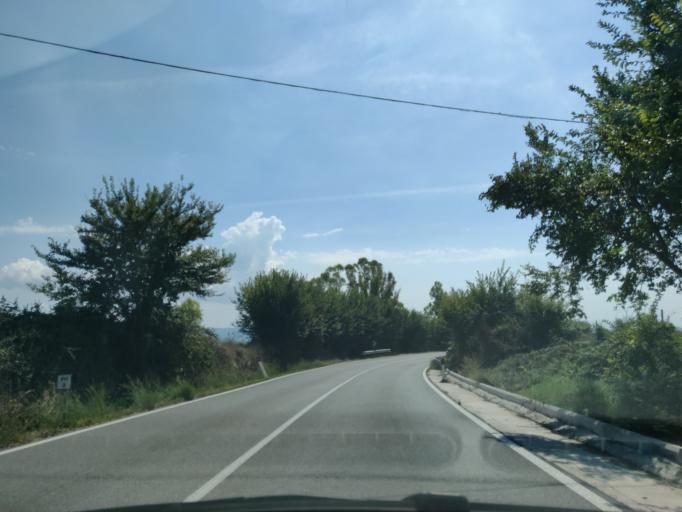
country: IT
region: Latium
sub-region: Provincia di Viterbo
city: Tarquinia
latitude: 42.2296
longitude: 11.7975
